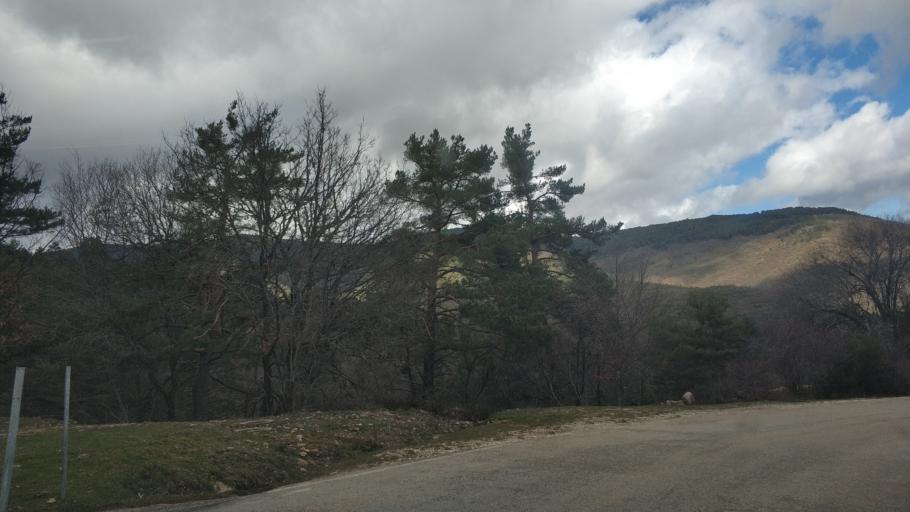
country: ES
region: Castille and Leon
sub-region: Provincia de Burgos
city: Neila
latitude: 42.0568
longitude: -3.0120
